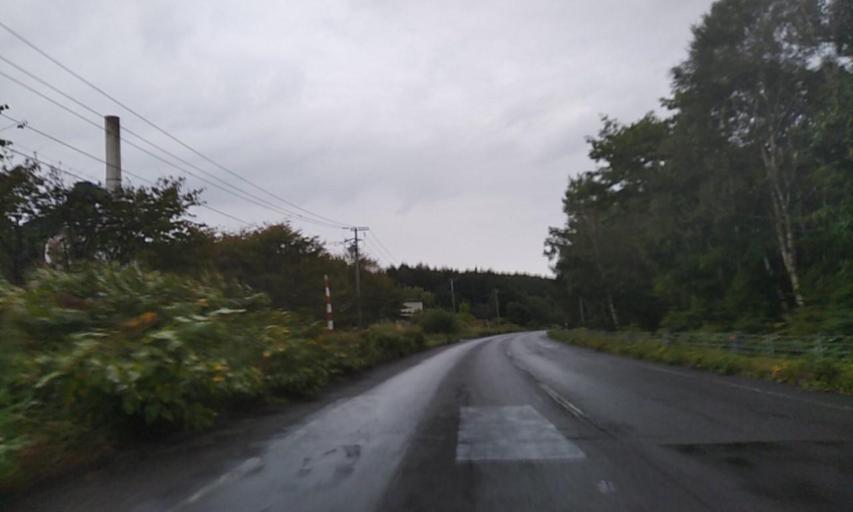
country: JP
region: Hokkaido
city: Mombetsu
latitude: 44.4821
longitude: 143.1033
